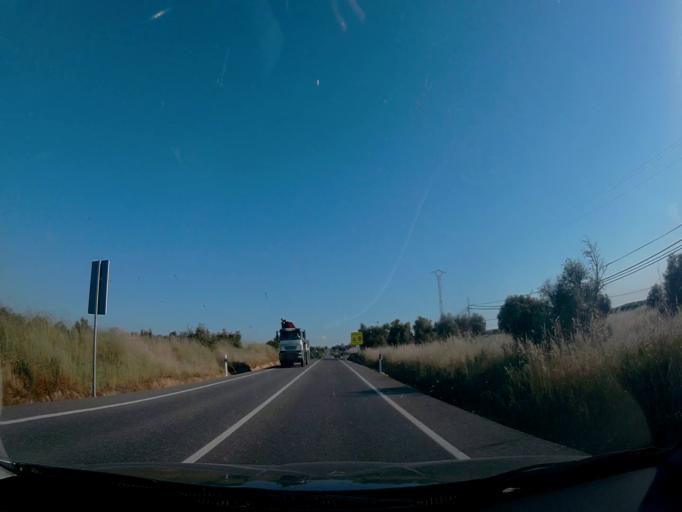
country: ES
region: Castille-La Mancha
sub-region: Province of Toledo
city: Escalona
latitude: 40.1456
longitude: -4.4031
